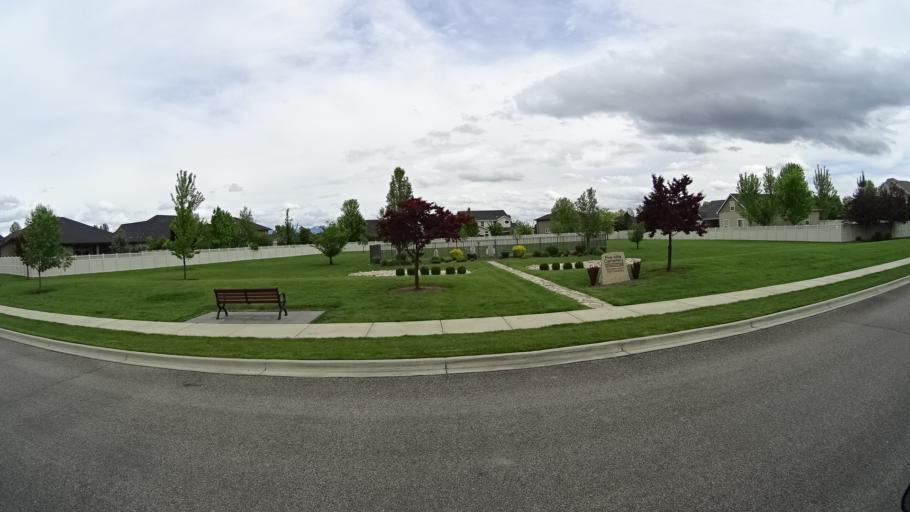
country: US
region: Idaho
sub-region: Ada County
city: Meridian
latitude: 43.6401
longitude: -116.4243
